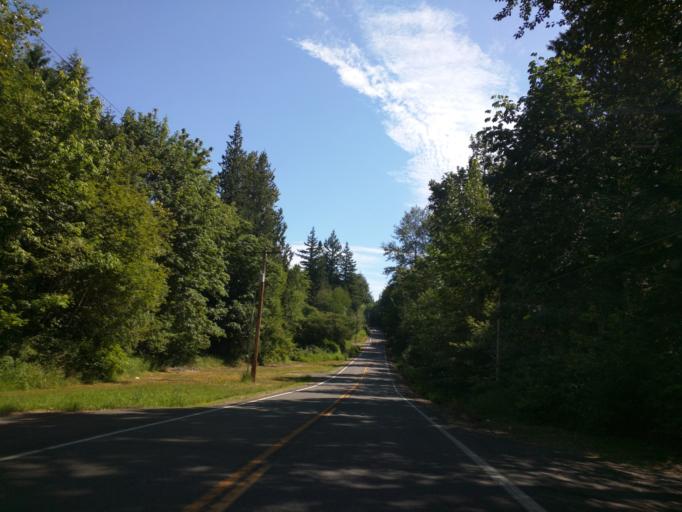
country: US
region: Washington
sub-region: Whatcom County
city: Sumas
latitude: 48.9674
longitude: -122.2143
